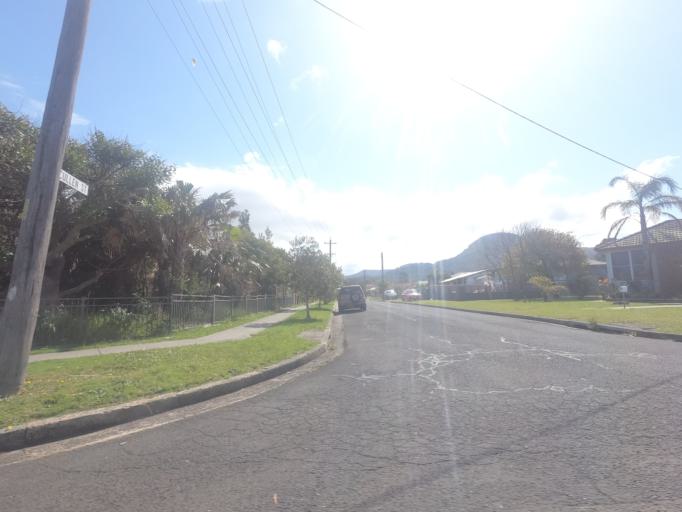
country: AU
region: New South Wales
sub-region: Wollongong
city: Cordeaux Heights
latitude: -34.4578
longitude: 150.8356
